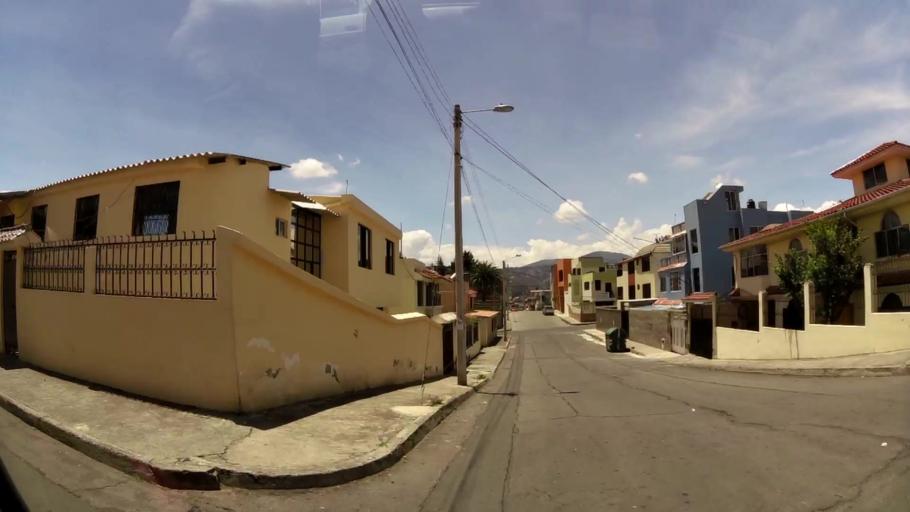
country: EC
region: Chimborazo
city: Riobamba
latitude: -1.6695
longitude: -78.6619
